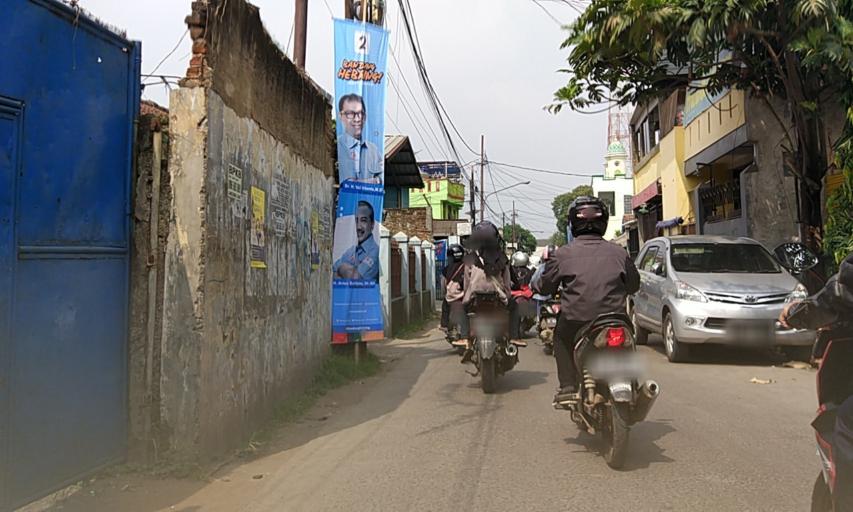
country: ID
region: West Java
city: Margahayukencana
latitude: -6.9373
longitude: 107.5832
